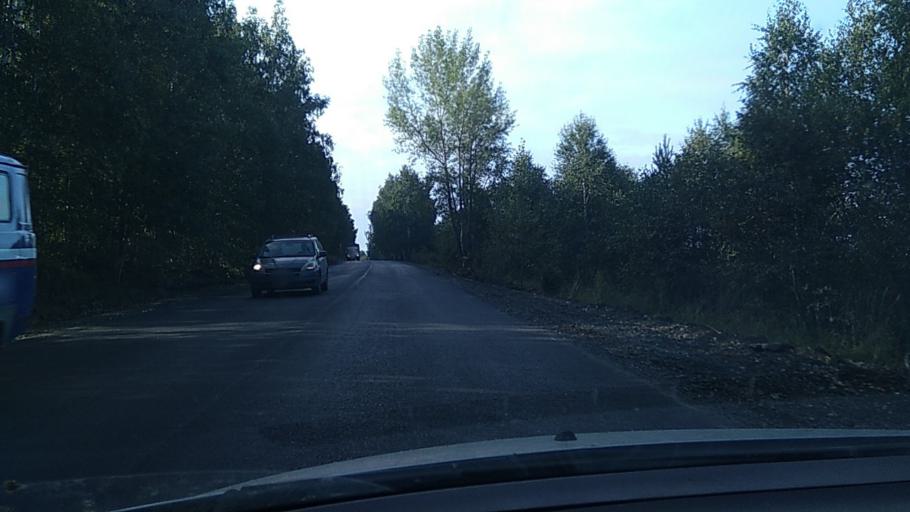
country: RU
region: Chelyabinsk
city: Karabash
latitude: 55.3719
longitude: 60.2490
